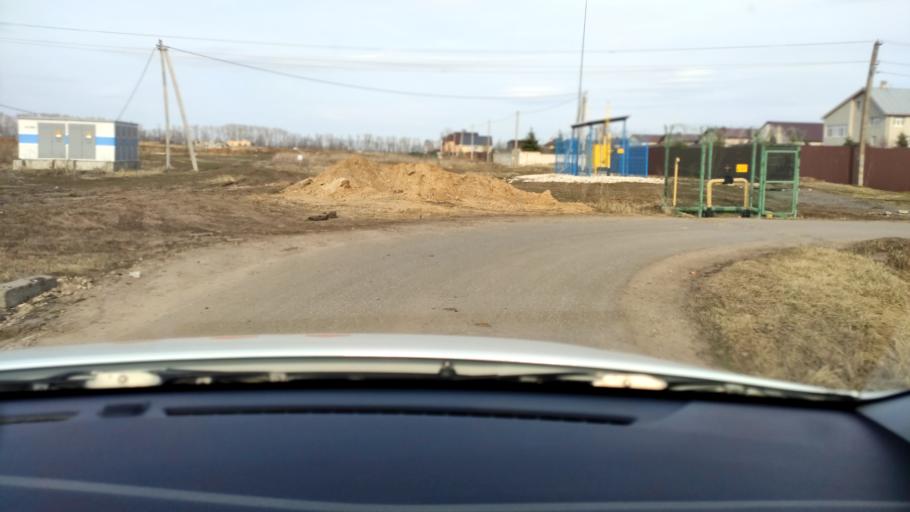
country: RU
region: Tatarstan
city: Stolbishchi
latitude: 55.6519
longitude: 49.3012
